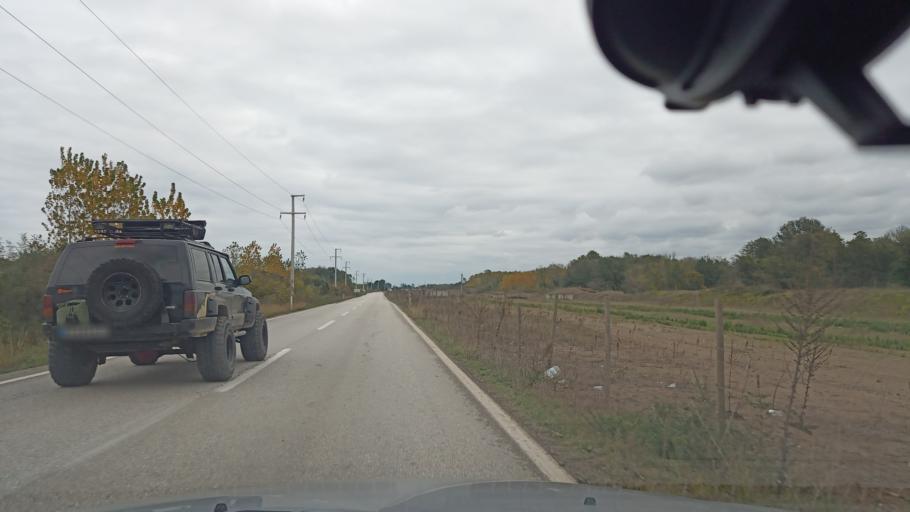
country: TR
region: Sakarya
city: Karasu
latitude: 41.1208
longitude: 30.5909
